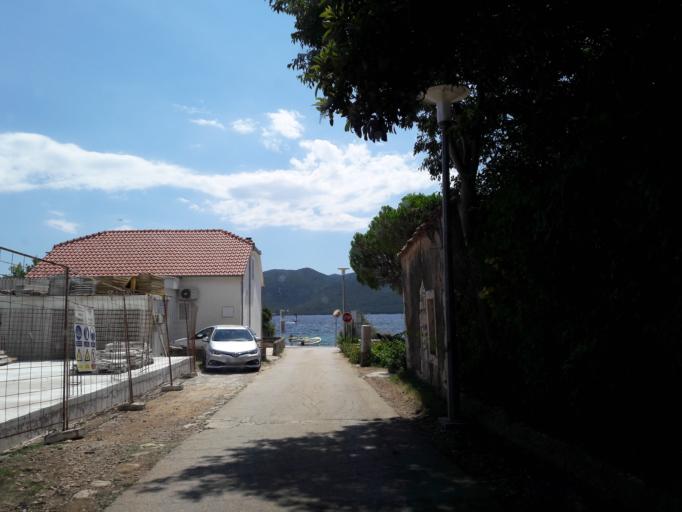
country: HR
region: Dubrovacko-Neretvanska
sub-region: Grad Korcula
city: Zrnovo
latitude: 42.9814
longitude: 17.1029
